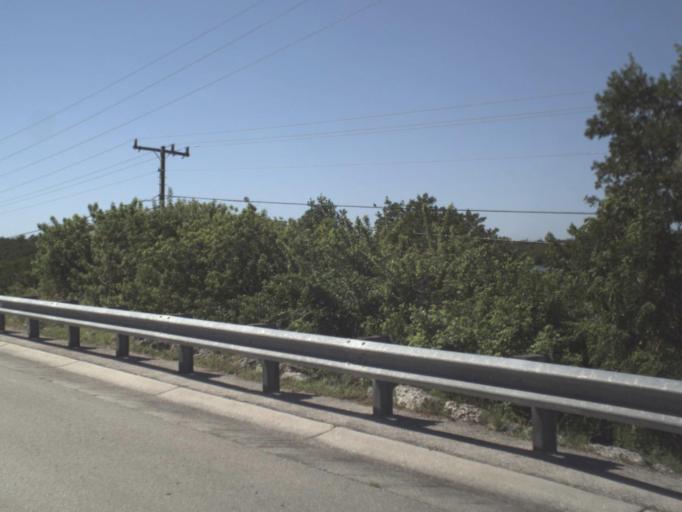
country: US
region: Florida
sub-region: Collier County
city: Marco
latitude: 25.9883
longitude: -81.7023
